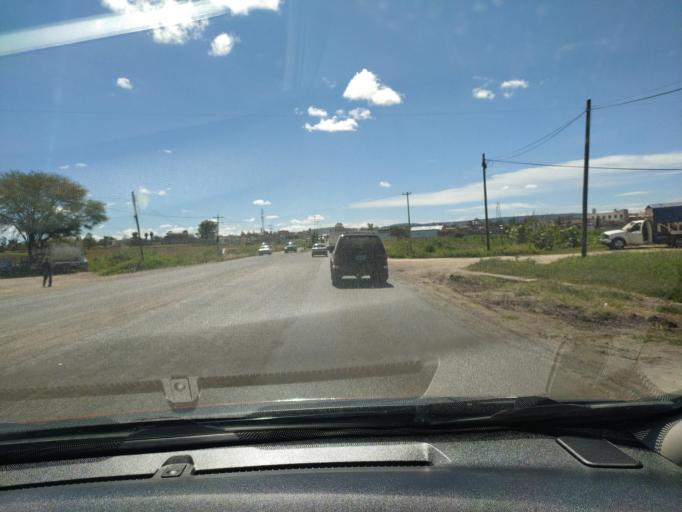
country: MX
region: Jalisco
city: San Miguel el Alto
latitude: 21.0369
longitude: -102.3976
